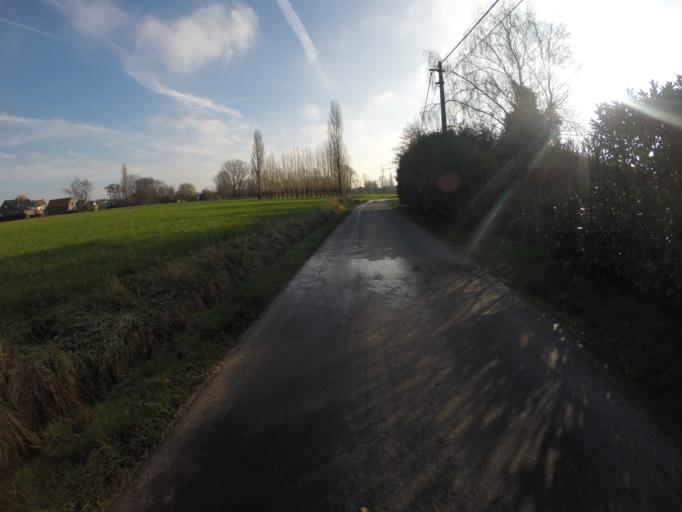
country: BE
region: Flanders
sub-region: Provincie Oost-Vlaanderen
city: Nevele
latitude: 51.0366
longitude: 3.5104
